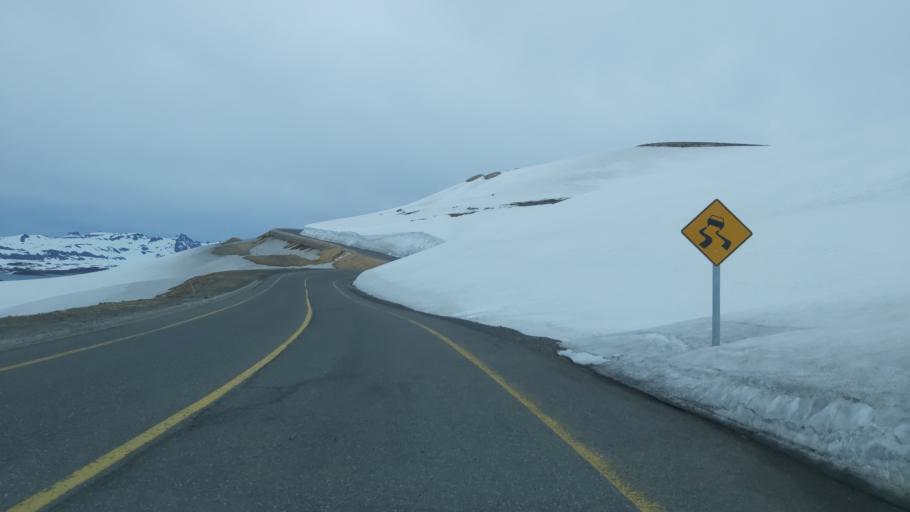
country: CL
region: Maule
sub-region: Provincia de Linares
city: Colbun
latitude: -36.0127
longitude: -70.4862
